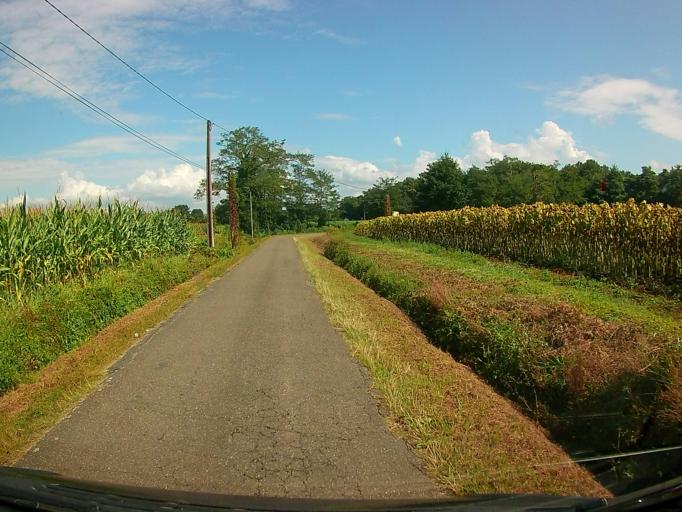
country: FR
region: Aquitaine
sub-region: Departement des Landes
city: Benesse-Maremne
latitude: 43.6249
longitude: -1.3808
